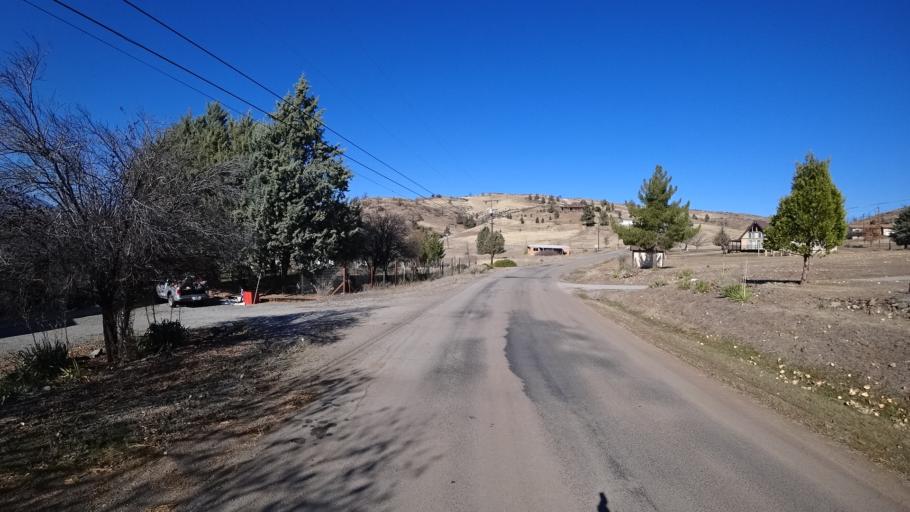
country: US
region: California
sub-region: Siskiyou County
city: Montague
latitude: 41.8988
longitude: -122.4867
